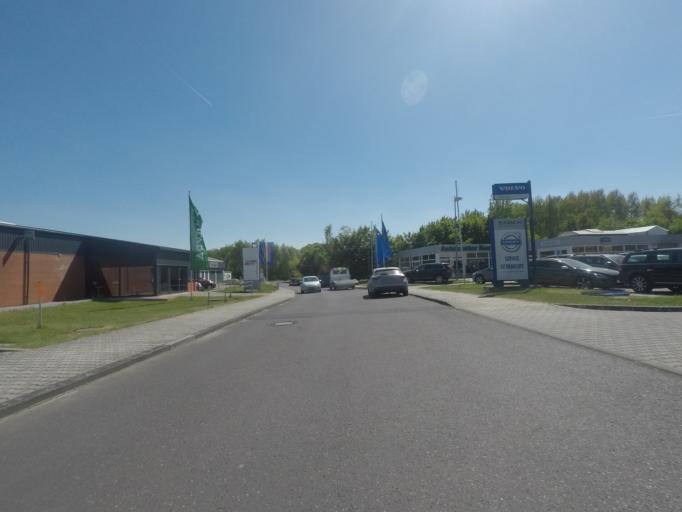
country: DE
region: Brandenburg
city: Melchow
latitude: 52.8481
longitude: 13.6913
